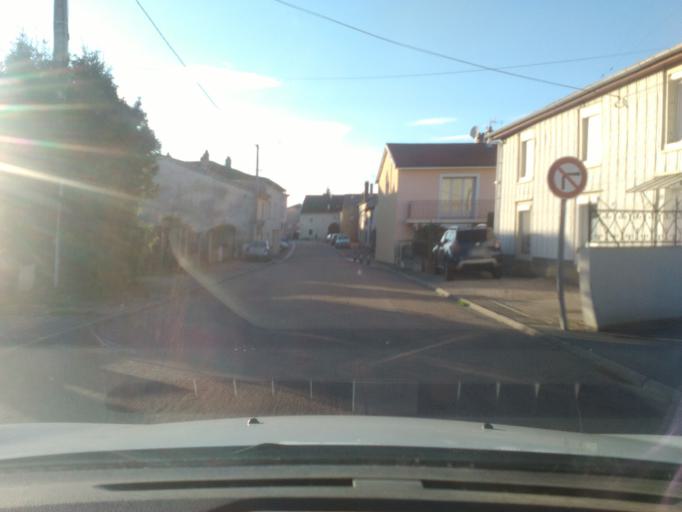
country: FR
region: Lorraine
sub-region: Departement des Vosges
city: Vincey
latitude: 48.3374
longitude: 6.3339
